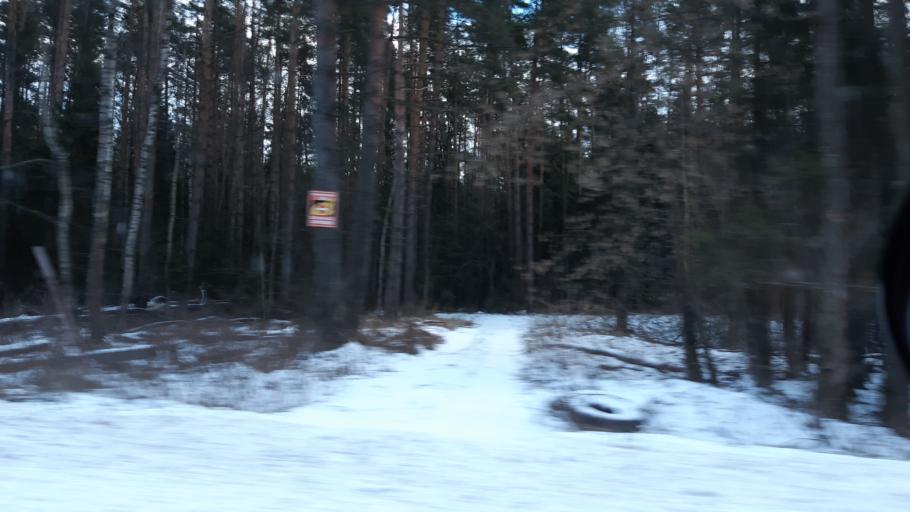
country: RU
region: Moskovskaya
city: Noginsk-9
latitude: 55.9802
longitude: 38.5440
